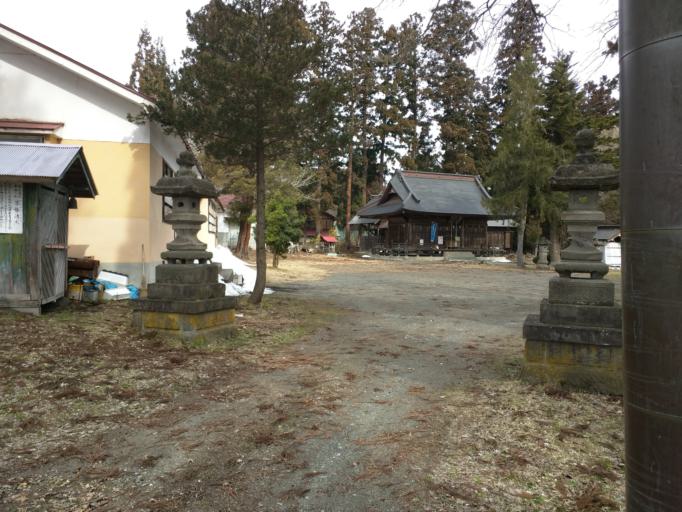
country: JP
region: Fukushima
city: Kitakata
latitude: 37.6443
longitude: 139.7727
